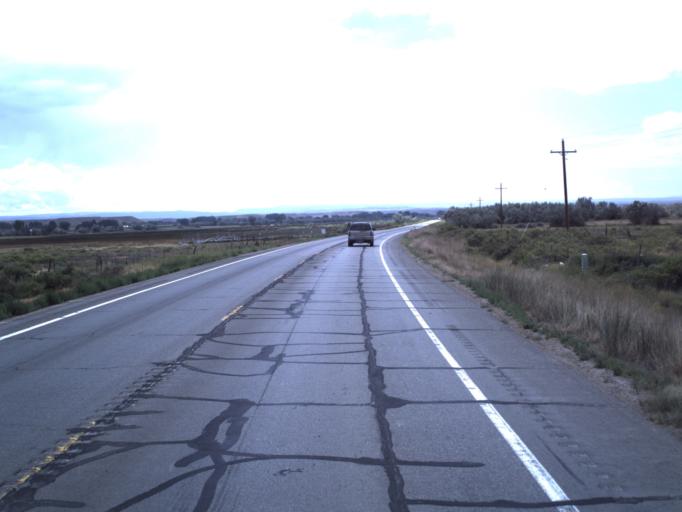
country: US
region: Utah
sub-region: Duchesne County
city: Roosevelt
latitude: 40.1657
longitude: -110.1520
